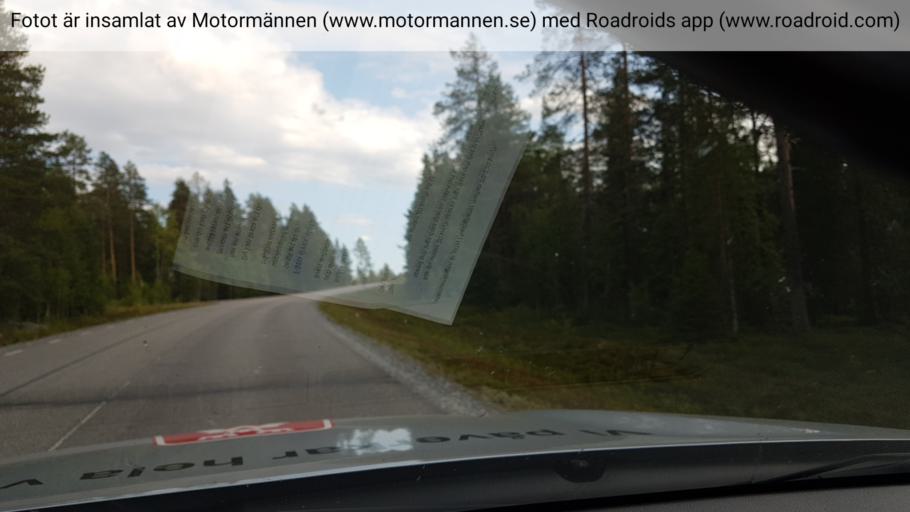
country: SE
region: Vaesterbotten
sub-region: Skelleftea Kommun
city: Storvik
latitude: 65.3365
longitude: 20.5687
